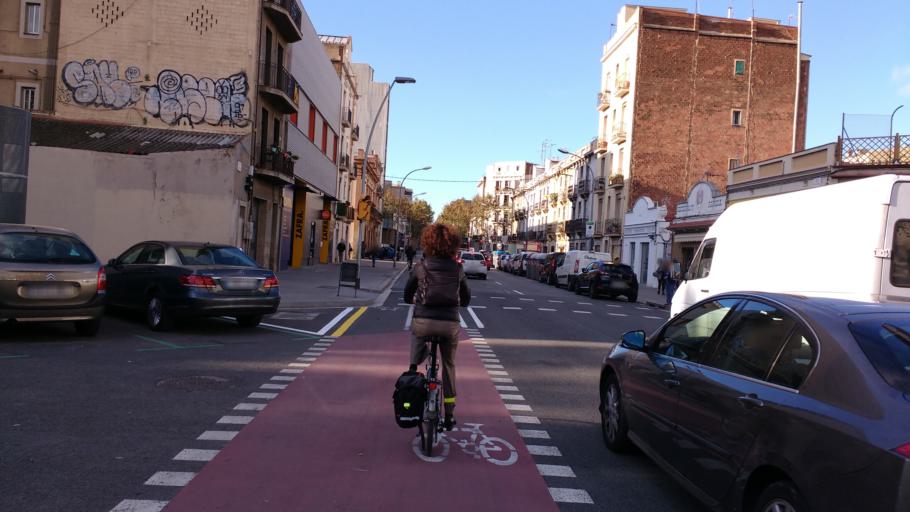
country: ES
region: Catalonia
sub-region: Provincia de Barcelona
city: Sant Marti
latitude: 41.3998
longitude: 2.1983
